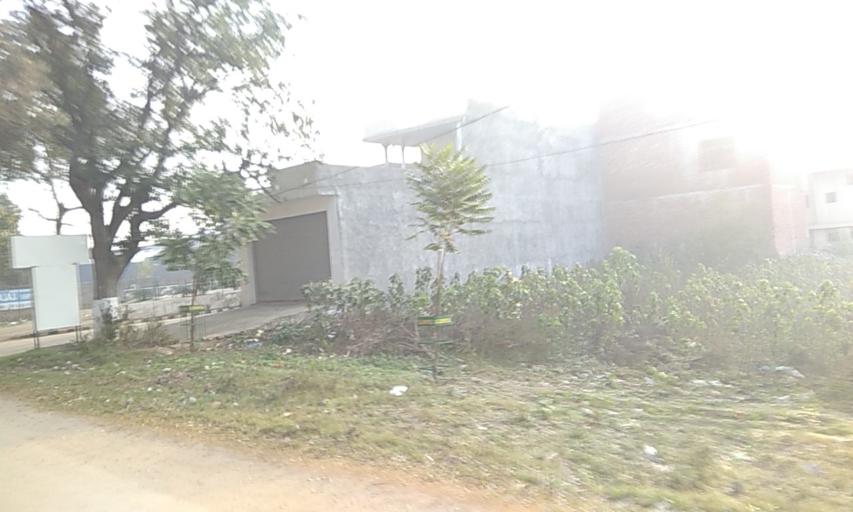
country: IN
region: Punjab
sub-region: Gurdaspur
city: Dhariwal
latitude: 31.9441
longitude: 75.3136
